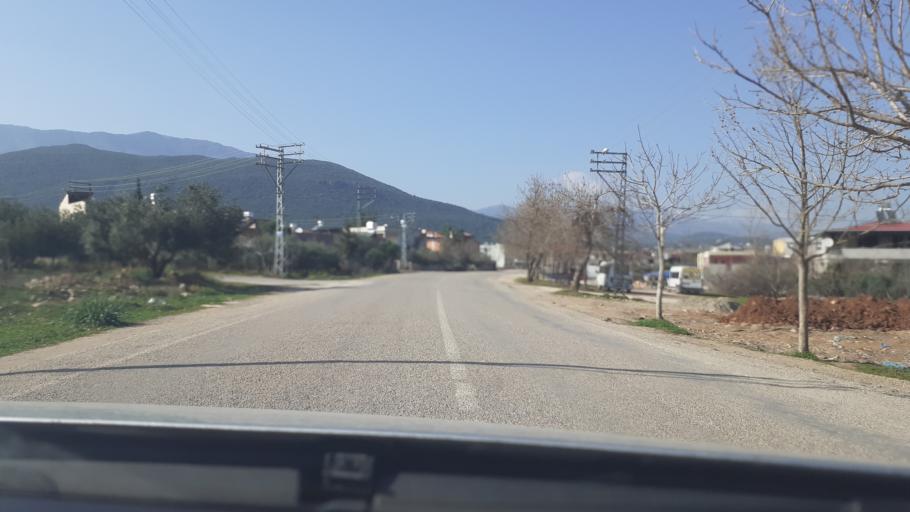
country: TR
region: Hatay
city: Aktepe
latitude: 36.7089
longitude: 36.4871
